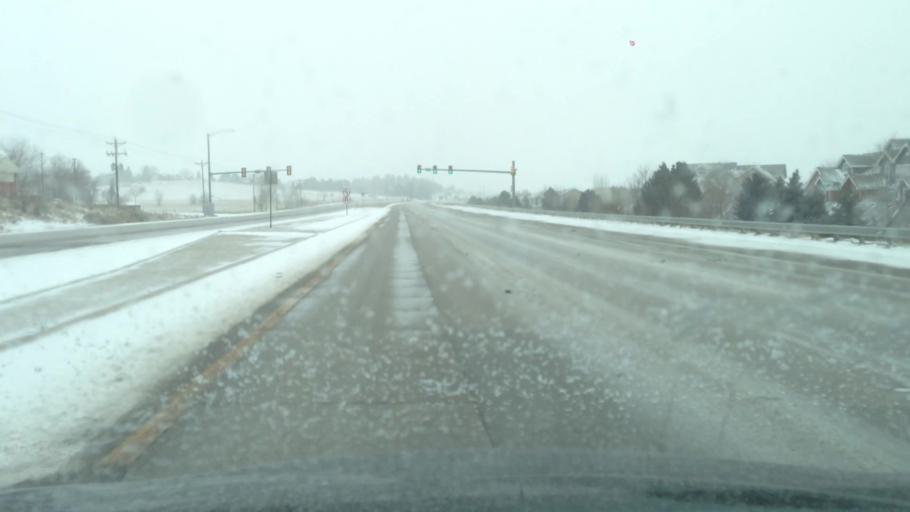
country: US
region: Colorado
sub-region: Arapahoe County
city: Dove Valley
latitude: 39.5856
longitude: -104.7966
